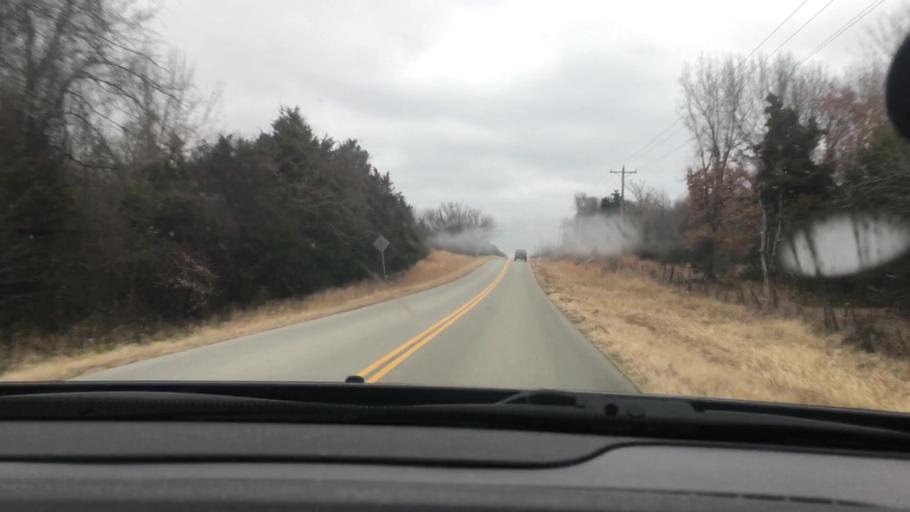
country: US
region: Oklahoma
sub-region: Atoka County
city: Atoka
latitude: 34.3319
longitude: -96.0754
